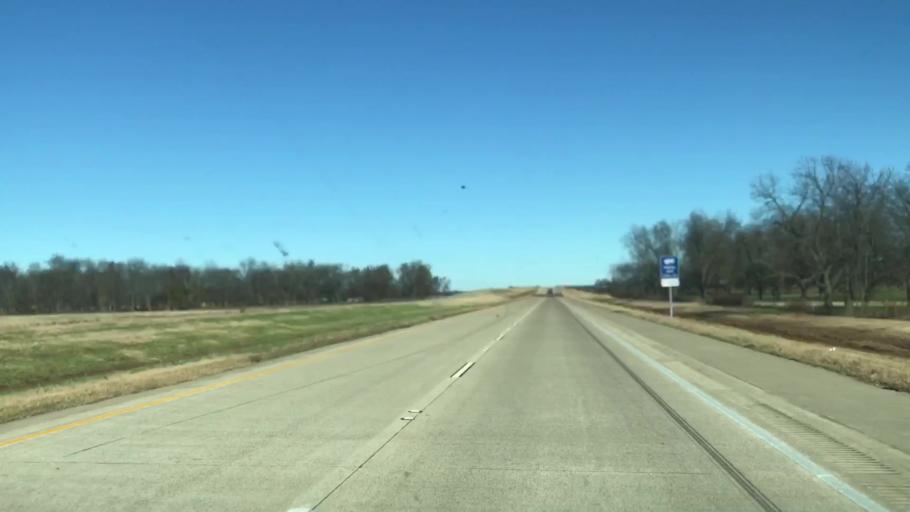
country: US
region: Louisiana
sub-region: Caddo Parish
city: Oil City
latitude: 32.7401
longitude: -93.8772
